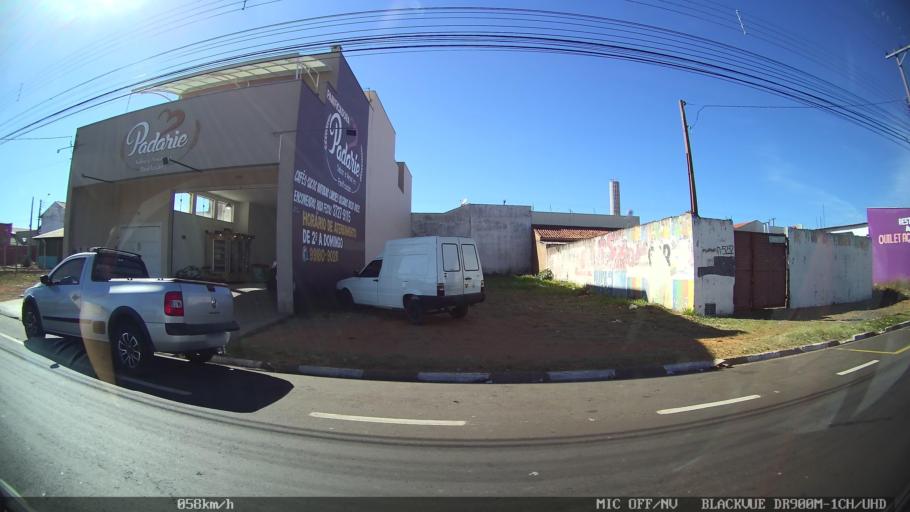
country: BR
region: Sao Paulo
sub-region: Franca
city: Franca
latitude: -20.5482
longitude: -47.3599
